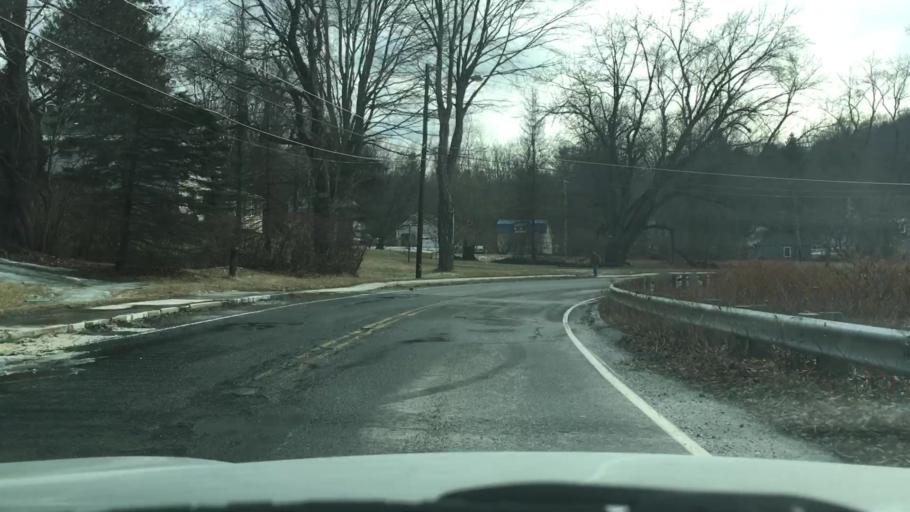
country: US
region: Massachusetts
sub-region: Berkshire County
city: Lee
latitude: 42.3129
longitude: -73.2456
